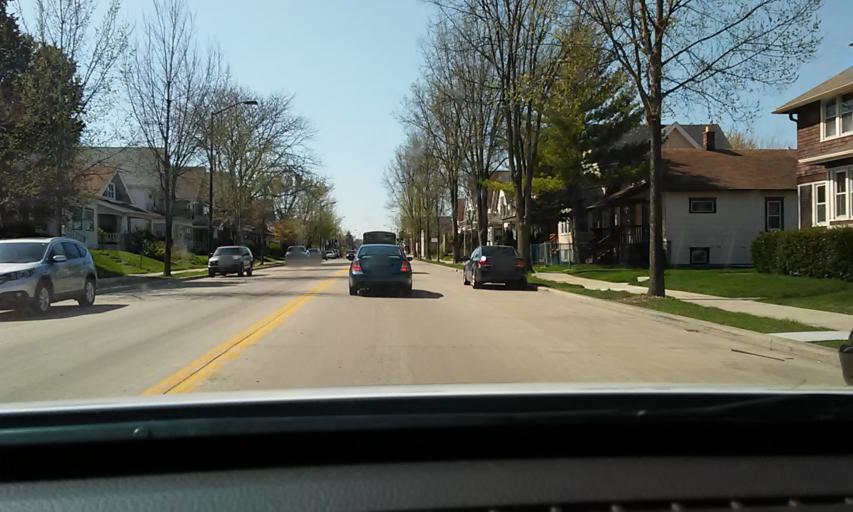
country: US
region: Wisconsin
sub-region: Milwaukee County
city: West Milwaukee
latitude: 43.0118
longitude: -87.9874
